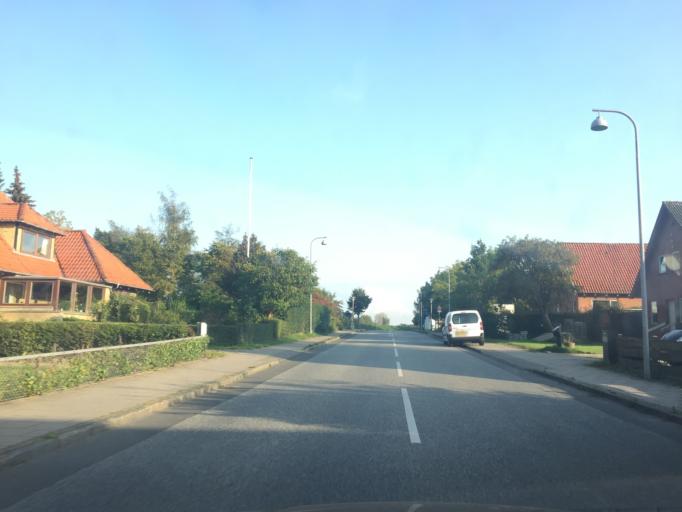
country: DK
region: Zealand
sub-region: Kalundborg Kommune
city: Svebolle
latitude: 55.6175
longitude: 11.2195
